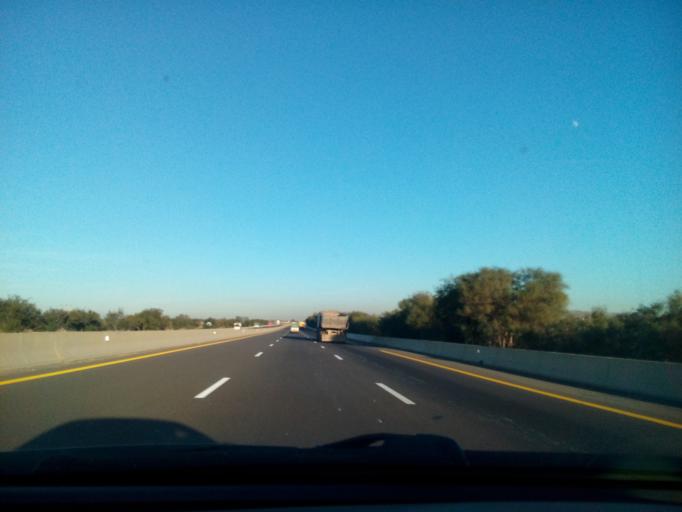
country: DZ
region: Relizane
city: Djidiouia
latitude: 35.9274
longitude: 0.7925
